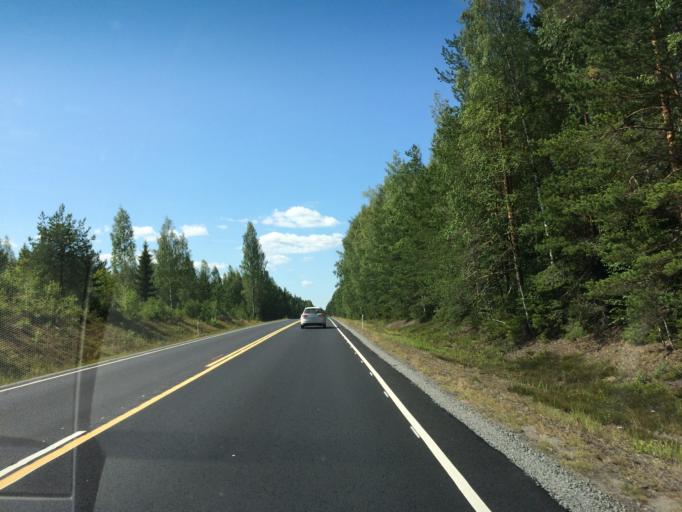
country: FI
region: Pirkanmaa
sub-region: Lounais-Pirkanmaa
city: Kiikoinen
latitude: 61.4748
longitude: 22.5503
